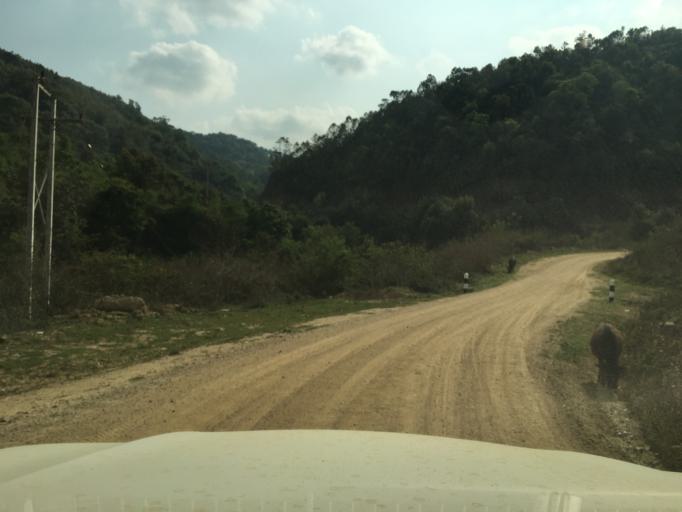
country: LA
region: Houaphan
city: Huameung
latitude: 20.2086
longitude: 103.8552
